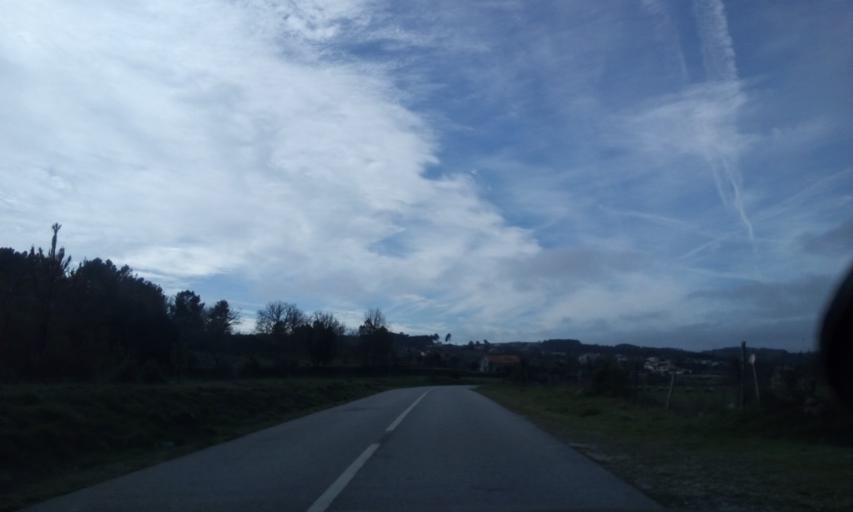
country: PT
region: Guarda
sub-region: Fornos de Algodres
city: Fornos de Algodres
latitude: 40.6631
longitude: -7.5307
